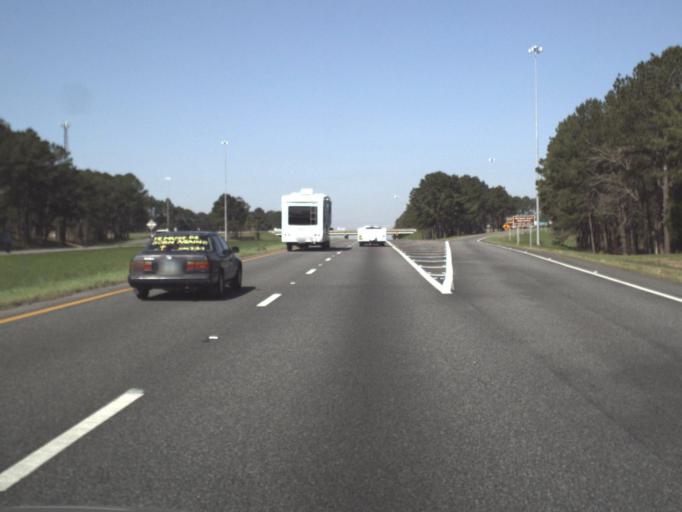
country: US
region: Florida
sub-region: Gadsden County
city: Quincy
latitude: 30.5370
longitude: -84.5900
